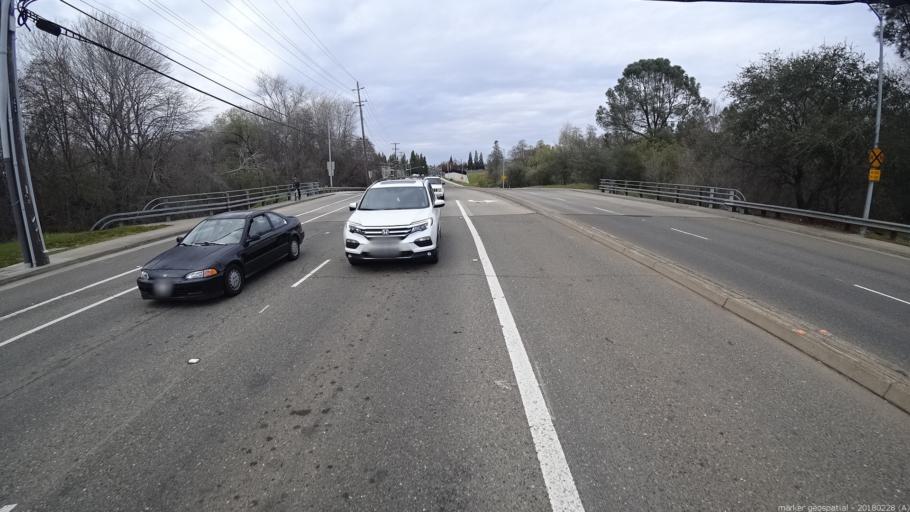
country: US
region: California
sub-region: Sacramento County
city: Folsom
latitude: 38.6569
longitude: -121.1687
